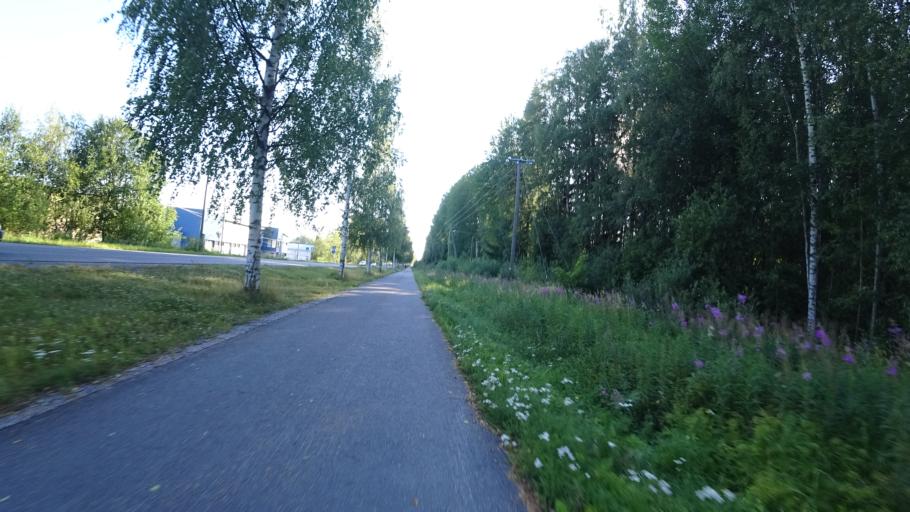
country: FI
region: Pirkanmaa
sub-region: Tampere
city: Nokia
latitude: 61.4738
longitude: 23.4731
